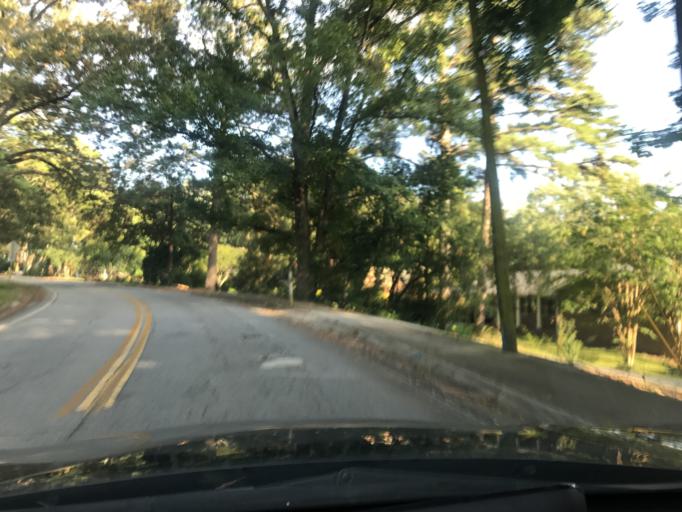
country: US
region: Georgia
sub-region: DeKalb County
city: Clarkston
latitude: 33.8245
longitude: -84.2702
